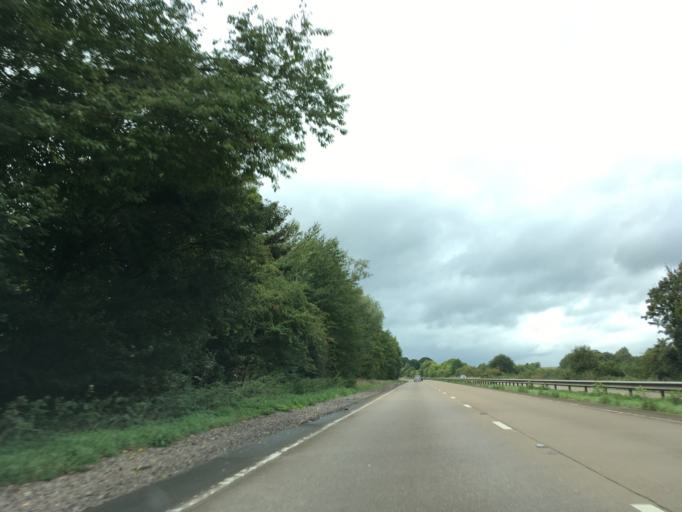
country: GB
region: Wales
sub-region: Monmouthshire
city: Llanarth
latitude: 51.7700
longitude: -2.8685
